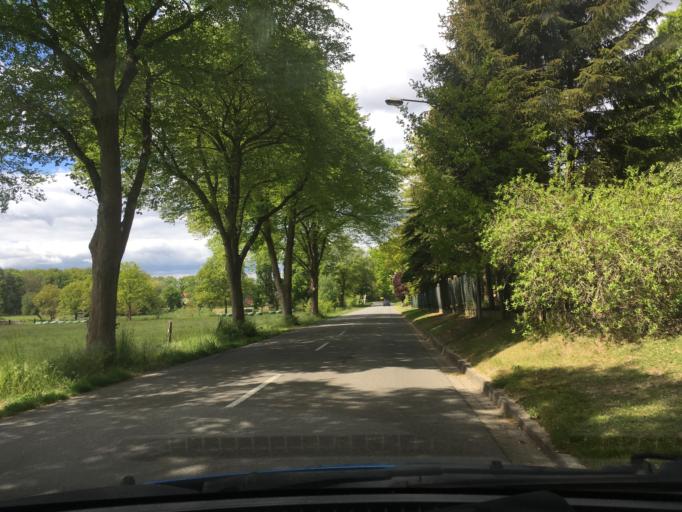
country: DE
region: Lower Saxony
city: Suderburg
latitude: 52.9176
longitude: 10.4645
